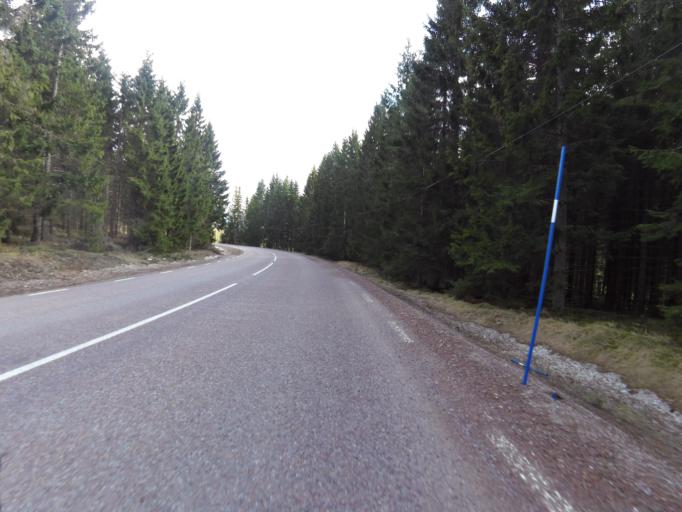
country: SE
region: Dalarna
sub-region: Avesta Kommun
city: Horndal
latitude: 60.3062
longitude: 16.2486
